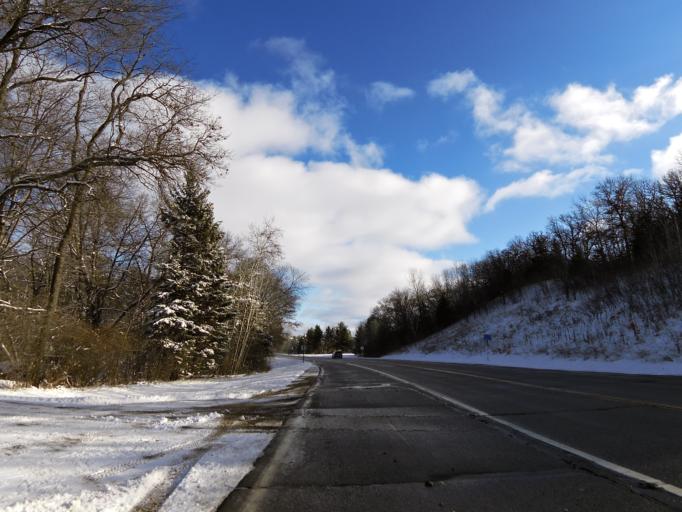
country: US
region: Minnesota
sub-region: Washington County
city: Lake Elmo
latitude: 44.9640
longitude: -92.8366
